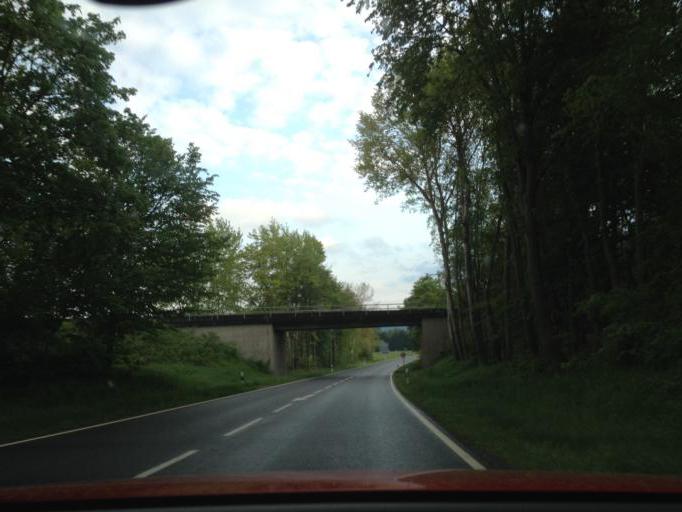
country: DE
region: Bavaria
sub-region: Upper Palatinate
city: Etzenricht
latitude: 49.6298
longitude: 12.1012
